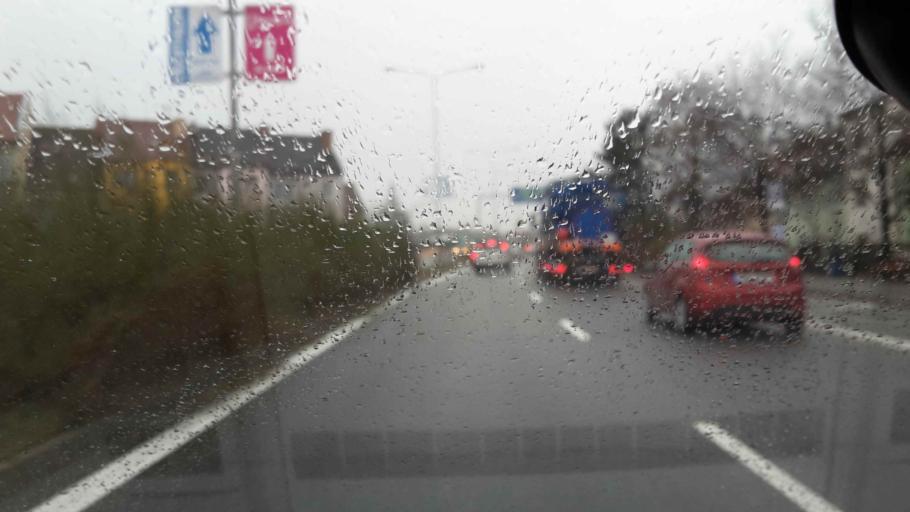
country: CZ
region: South Moravian
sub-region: Mesto Brno
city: Brno
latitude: 49.1922
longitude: 16.6478
